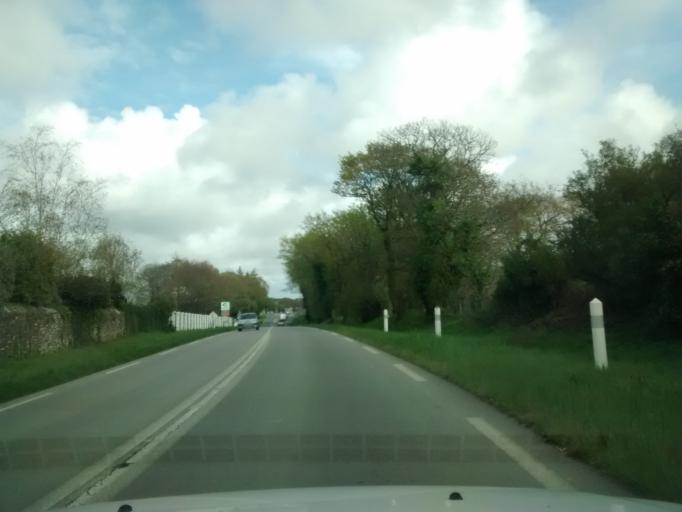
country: FR
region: Brittany
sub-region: Departement du Morbihan
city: Gestel
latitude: 47.7804
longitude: -3.4404
